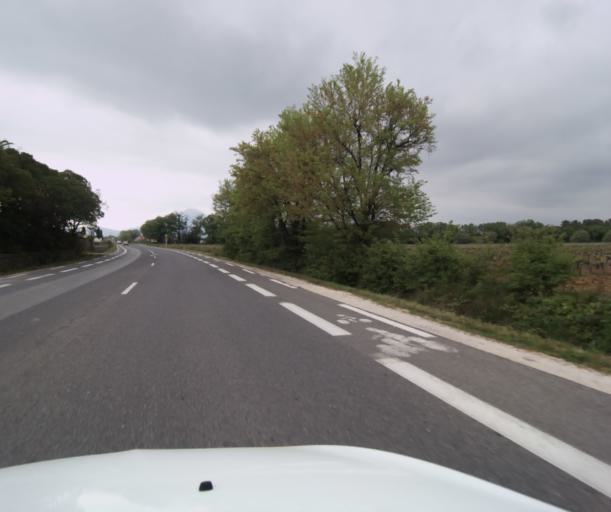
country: FR
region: Provence-Alpes-Cote d'Azur
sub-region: Departement du Var
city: La Crau
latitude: 43.1276
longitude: 6.0823
